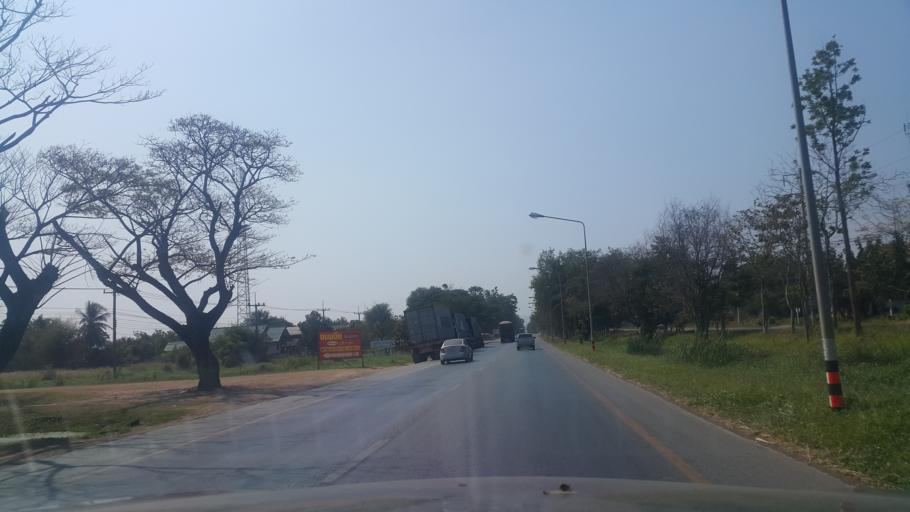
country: TH
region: Nakhon Ratchasima
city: Pak Thong Chai
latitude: 14.5580
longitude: 101.9757
